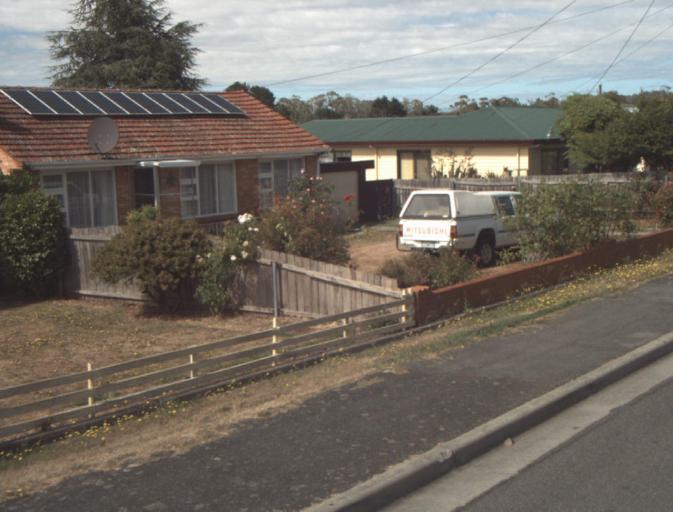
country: AU
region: Tasmania
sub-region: Launceston
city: Summerhill
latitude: -41.4683
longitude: 147.1264
